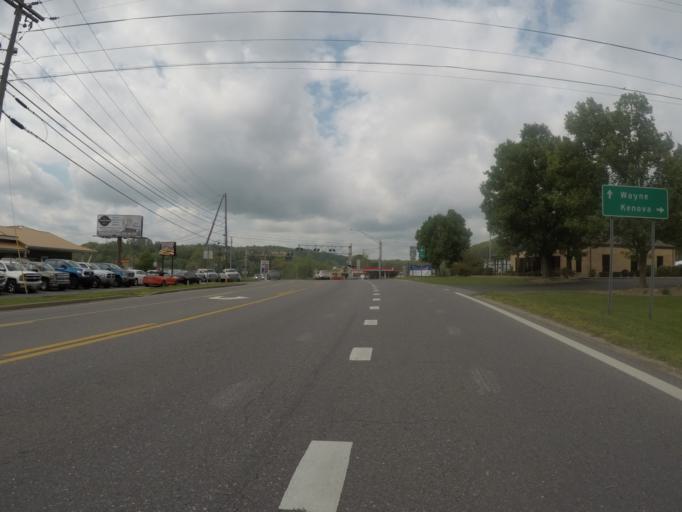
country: US
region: West Virginia
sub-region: Wayne County
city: Lavalette
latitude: 38.3365
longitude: -82.4538
